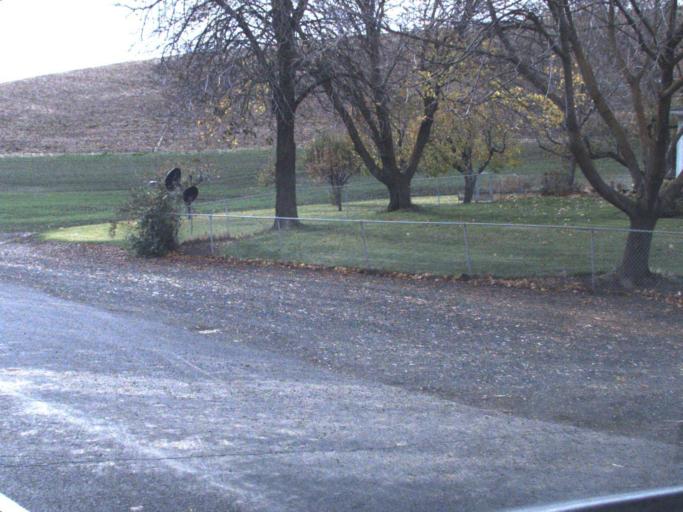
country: US
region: Washington
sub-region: Whitman County
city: Colfax
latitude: 46.8110
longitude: -117.5363
